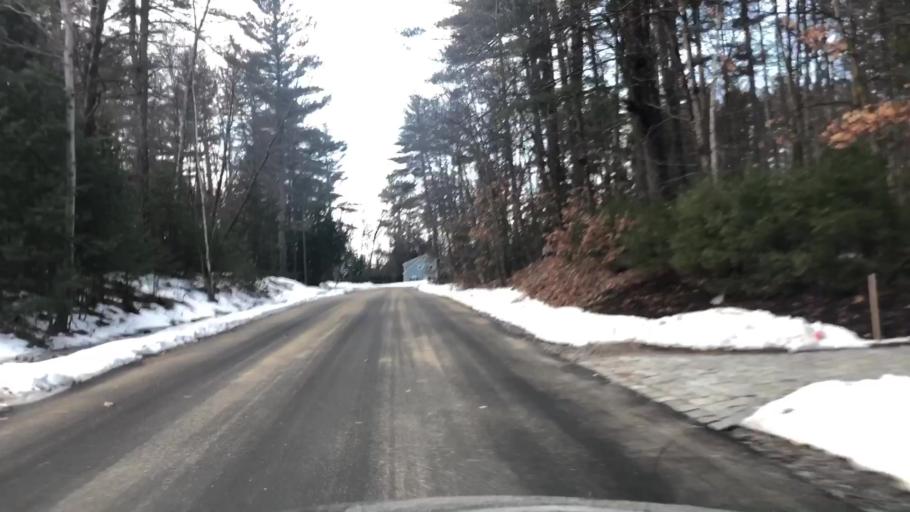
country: US
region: New Hampshire
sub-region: Hillsborough County
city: Milford
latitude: 42.8544
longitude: -71.6289
